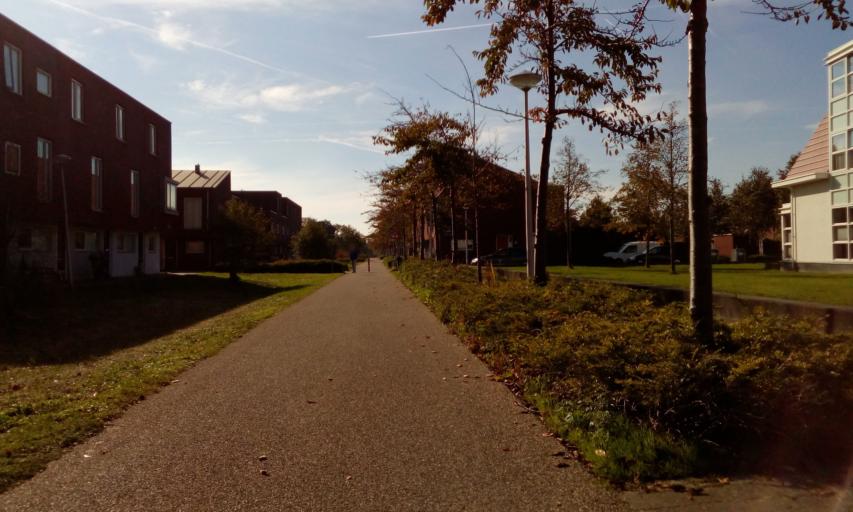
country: NL
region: Utrecht
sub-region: Stichtse Vecht
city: Spechtenkamp
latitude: 52.0829
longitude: 5.0233
